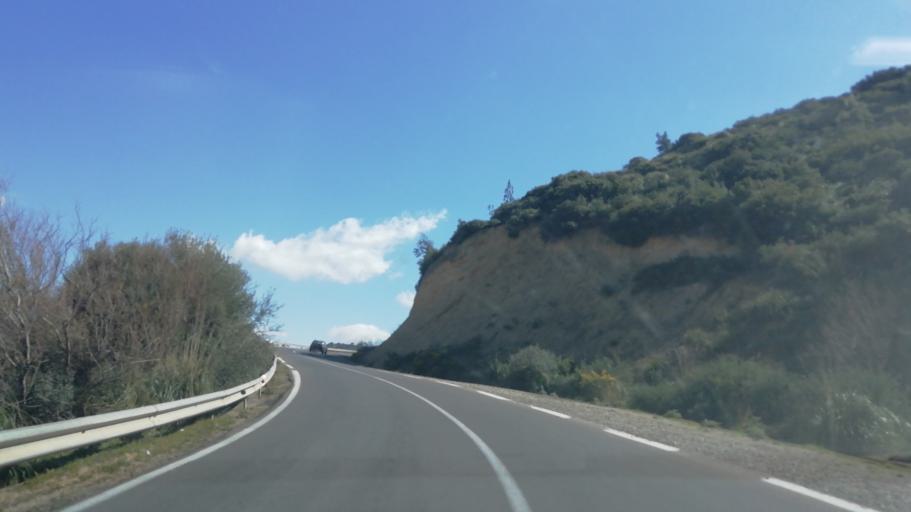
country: DZ
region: Mascara
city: Mascara
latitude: 35.4819
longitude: 0.1581
